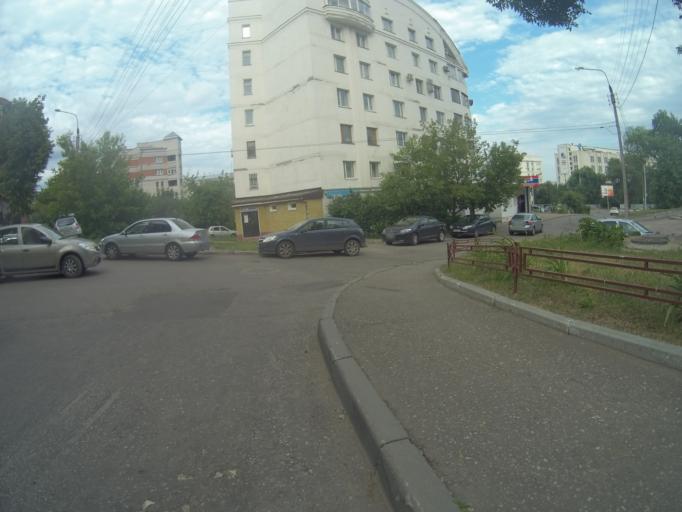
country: RU
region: Vladimir
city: Vladimir
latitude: 56.1376
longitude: 40.3931
